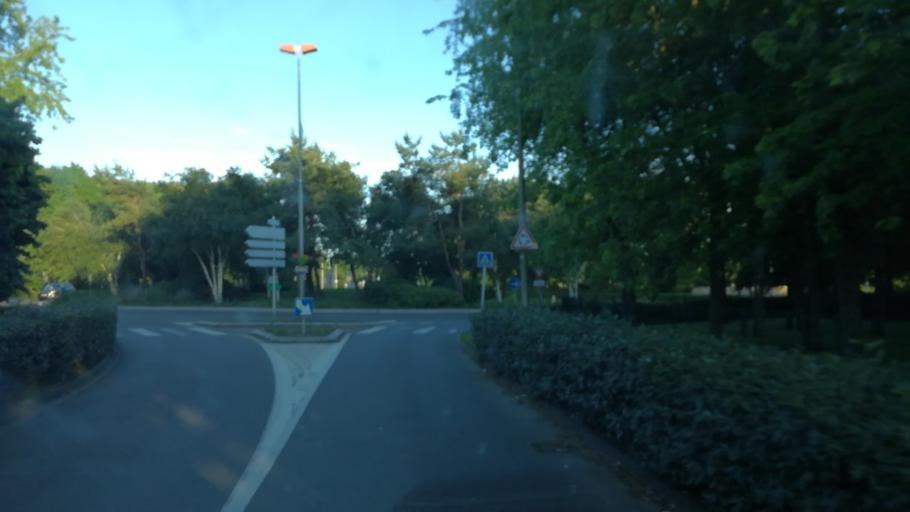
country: FR
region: Ile-de-France
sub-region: Departement des Yvelines
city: Elancourt
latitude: 48.7687
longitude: 1.9630
